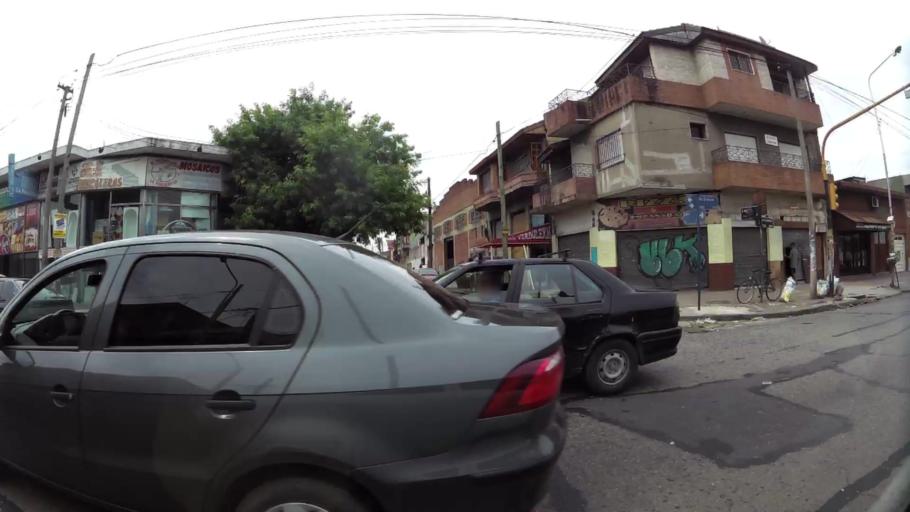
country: AR
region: Buenos Aires
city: San Justo
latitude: -34.6857
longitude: -58.5194
